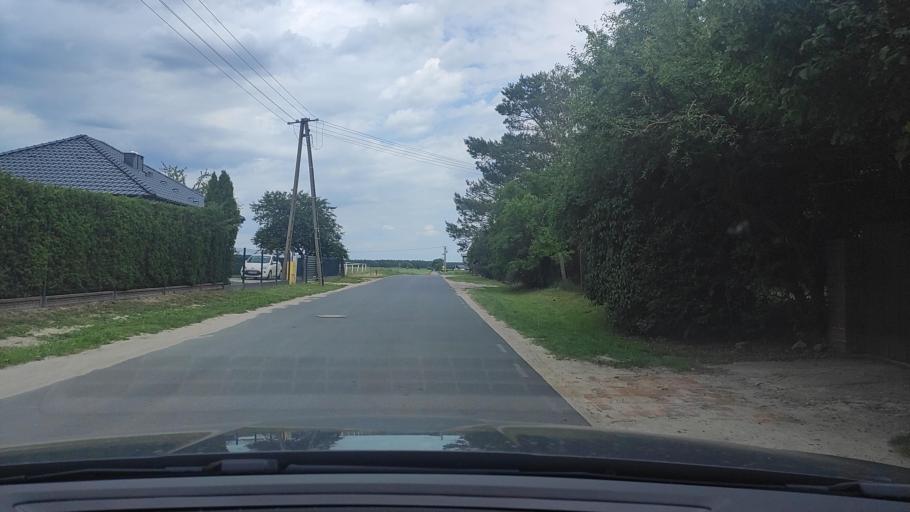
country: PL
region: Greater Poland Voivodeship
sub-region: Powiat poznanski
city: Kostrzyn
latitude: 52.4808
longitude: 17.1888
